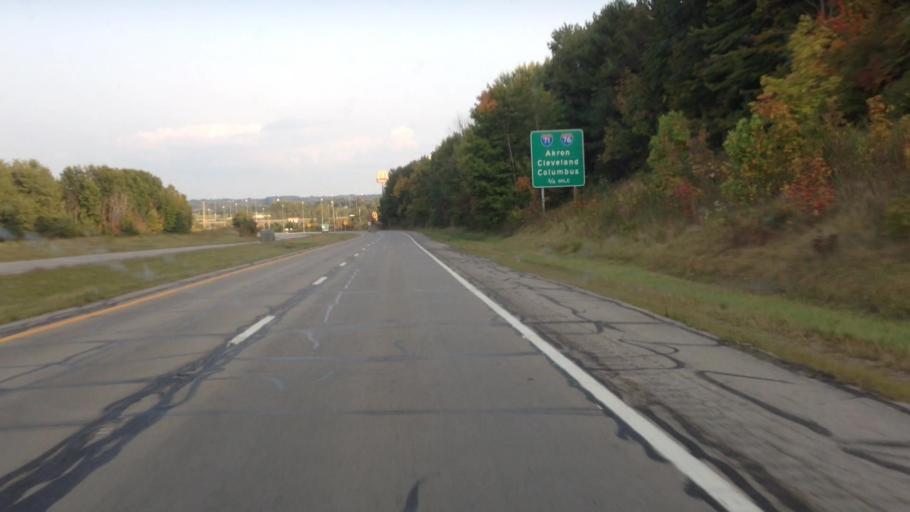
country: US
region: Ohio
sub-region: Medina County
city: Westfield Center
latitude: 41.0333
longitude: -81.9134
